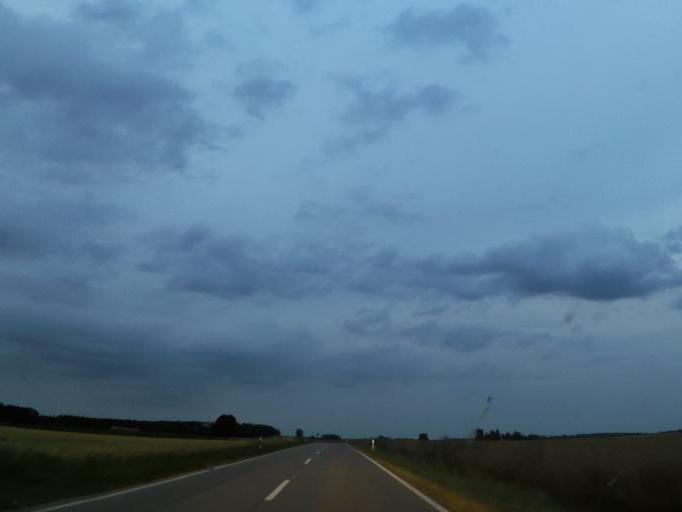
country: DE
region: Bavaria
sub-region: Upper Bavaria
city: Pastetten
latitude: 48.2086
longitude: 11.9629
